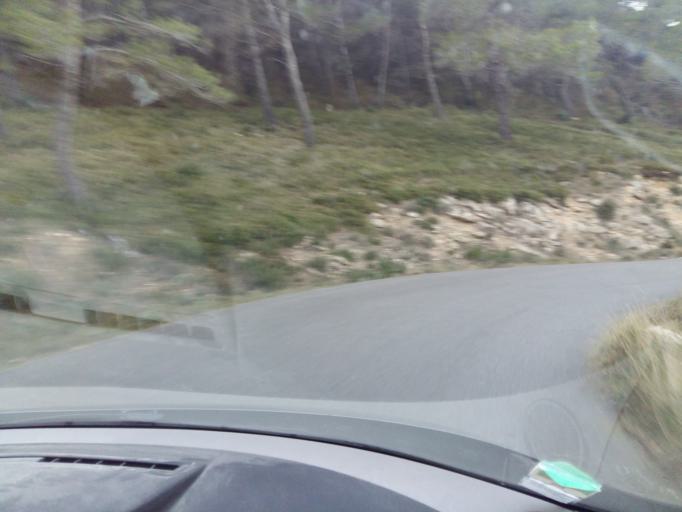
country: FR
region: Provence-Alpes-Cote d'Azur
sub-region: Departement des Bouches-du-Rhone
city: Maussane-les-Alpilles
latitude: 43.7581
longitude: 4.7939
